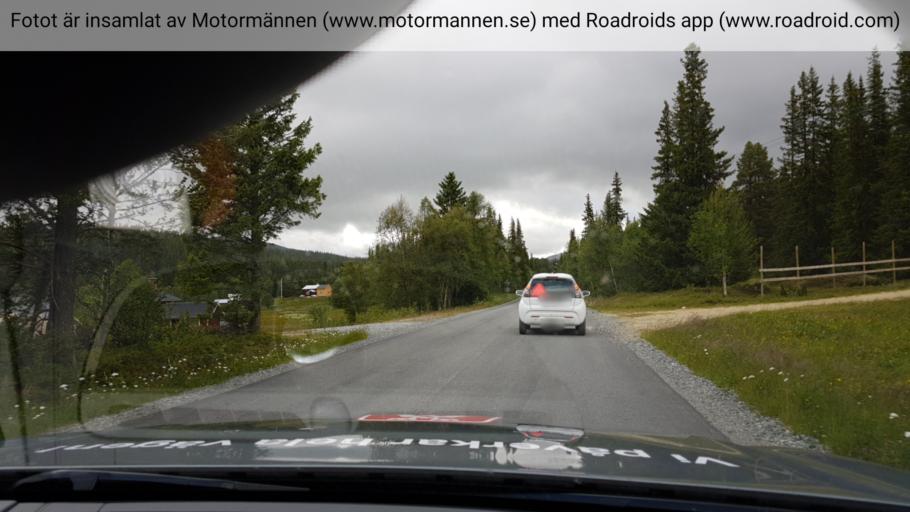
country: SE
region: Jaemtland
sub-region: Are Kommun
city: Are
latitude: 62.8544
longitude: 12.7716
